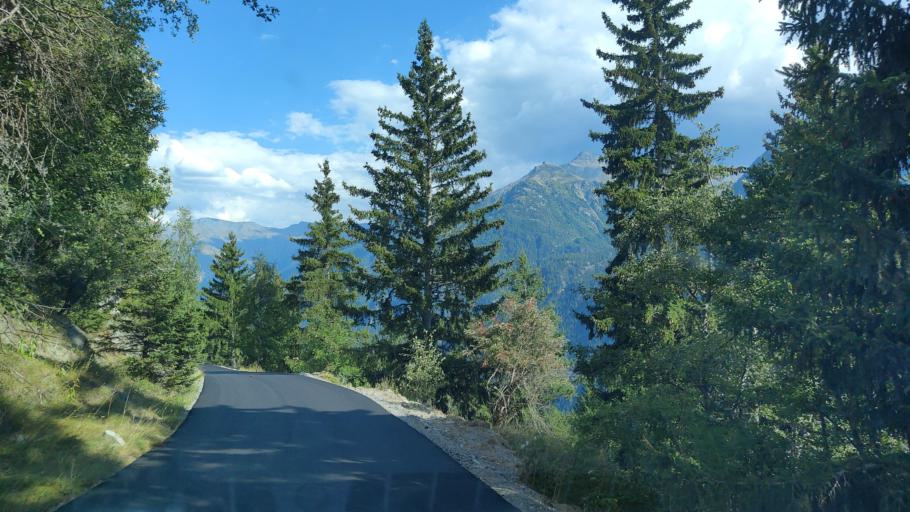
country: FR
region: Rhone-Alpes
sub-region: Departement de la Savoie
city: Val Thorens
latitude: 45.2201
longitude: 6.5560
